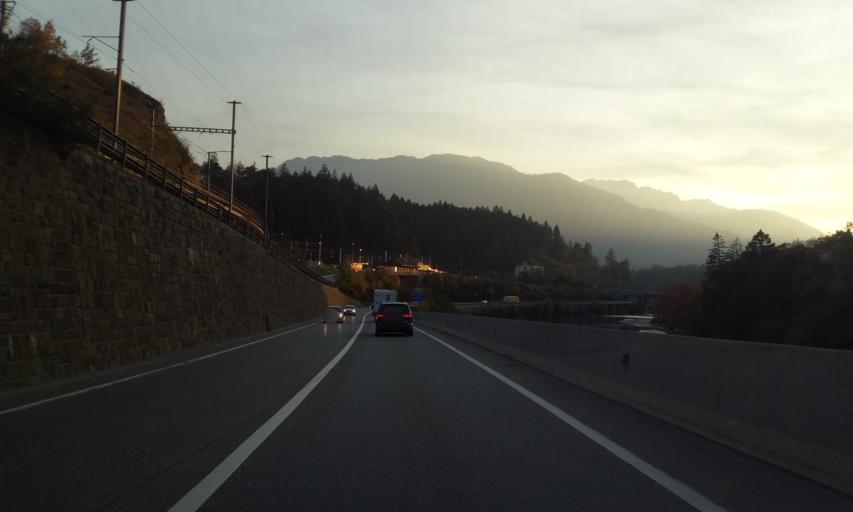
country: CH
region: Grisons
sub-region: Imboden District
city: Tamins
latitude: 46.8270
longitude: 9.4155
